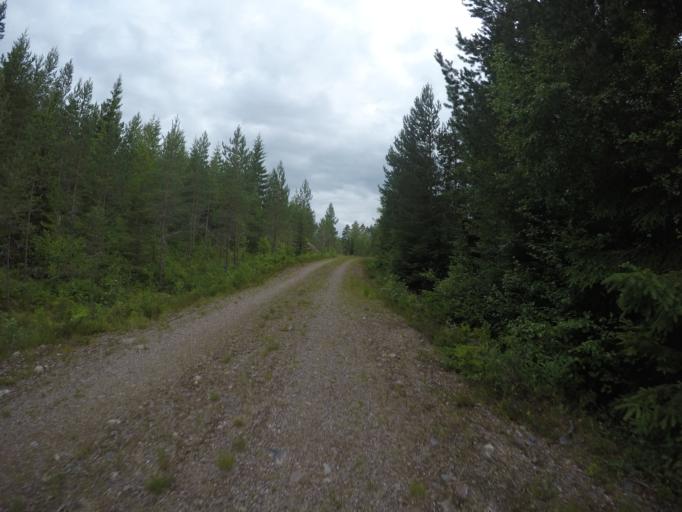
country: SE
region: Vaermland
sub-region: Filipstads Kommun
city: Lesjofors
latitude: 60.2114
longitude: 14.2613
